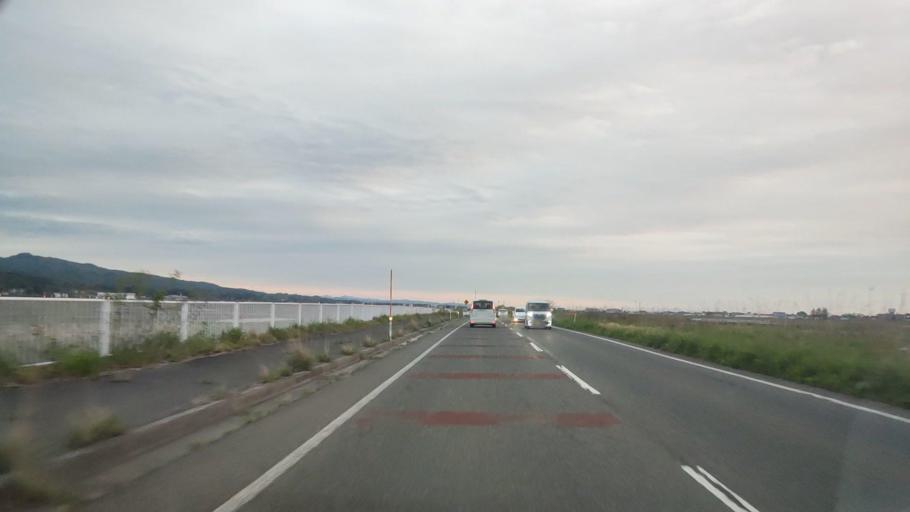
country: JP
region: Niigata
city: Niitsu-honcho
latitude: 37.7625
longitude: 139.0963
